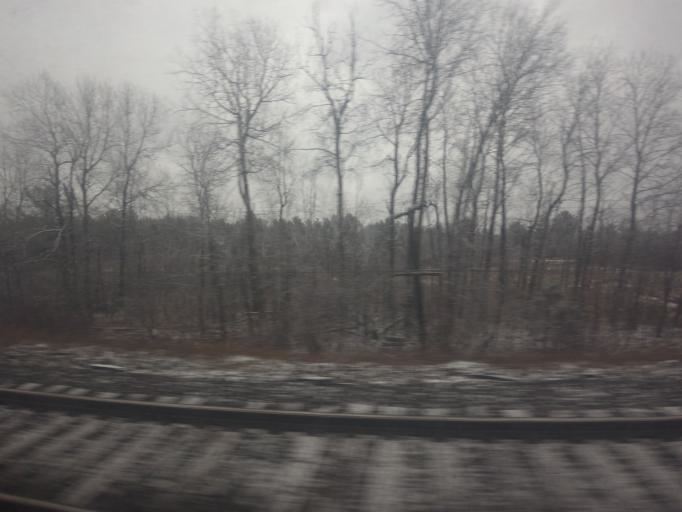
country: US
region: New York
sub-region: Jefferson County
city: Alexandria Bay
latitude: 44.4318
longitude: -75.9708
